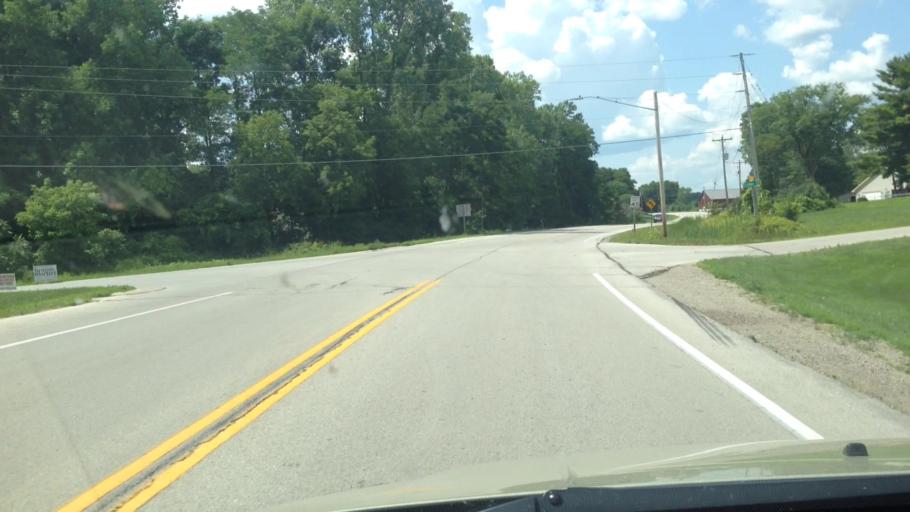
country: US
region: Wisconsin
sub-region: Brown County
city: Suamico
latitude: 44.6468
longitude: -88.1176
